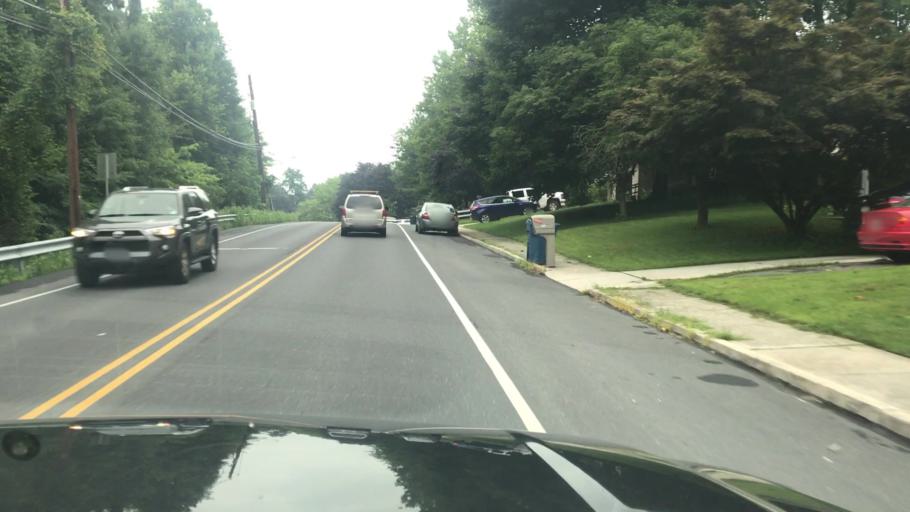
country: US
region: Pennsylvania
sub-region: Cumberland County
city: Shiremanstown
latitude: 40.2560
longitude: -76.9592
